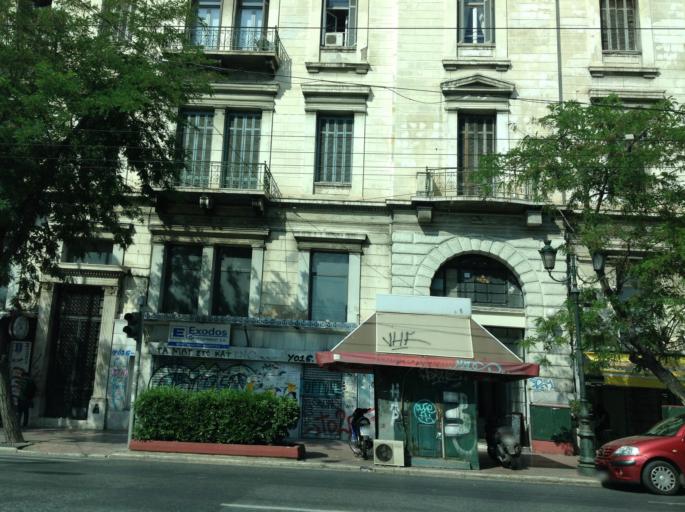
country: GR
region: Attica
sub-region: Nomarchia Athinas
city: Athens
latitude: 37.9822
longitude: 23.7315
